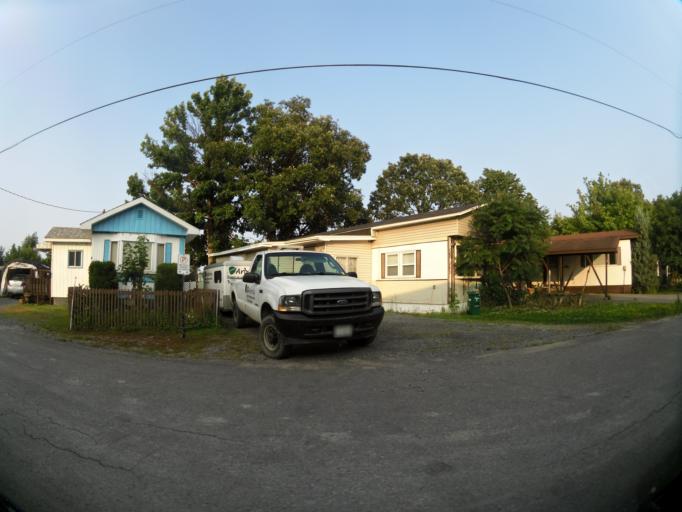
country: CA
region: Quebec
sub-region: Outaouais
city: Gatineau
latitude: 45.4879
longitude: -75.4918
